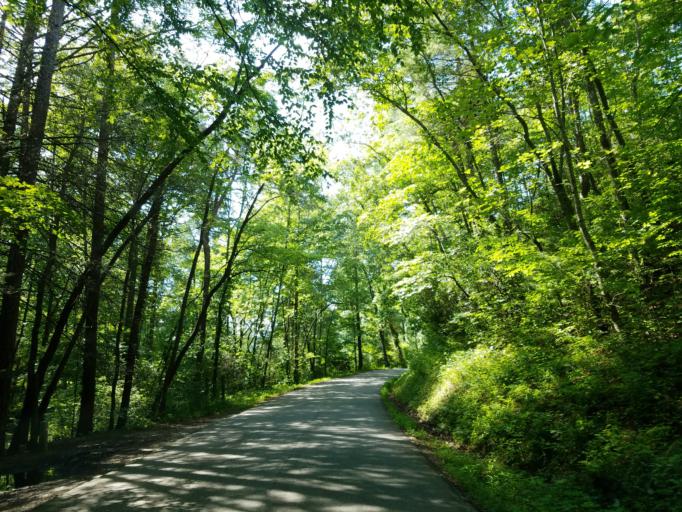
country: US
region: Georgia
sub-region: Dawson County
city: Dawsonville
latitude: 34.5650
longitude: -84.1461
